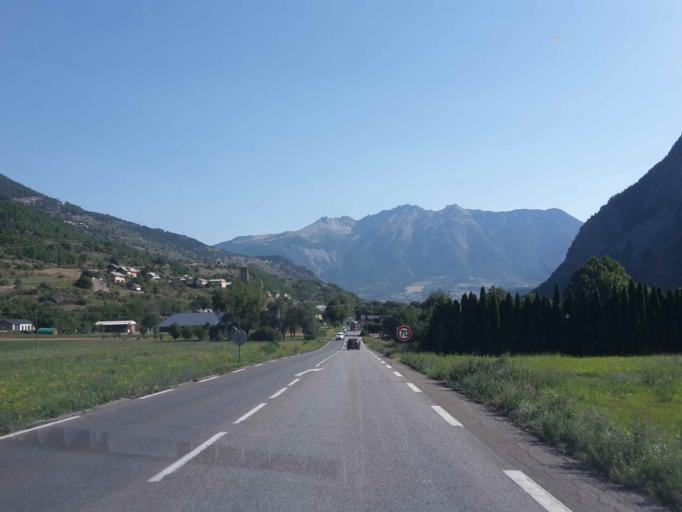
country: FR
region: Provence-Alpes-Cote d'Azur
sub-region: Departement des Hautes-Alpes
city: Guillestre
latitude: 44.6432
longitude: 6.5726
